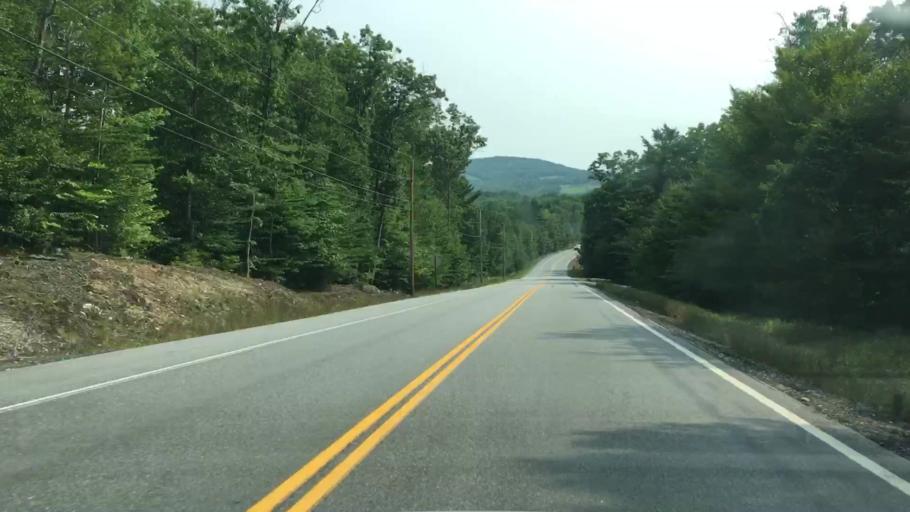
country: US
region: Maine
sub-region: Oxford County
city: Paris
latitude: 44.2535
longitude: -70.4382
